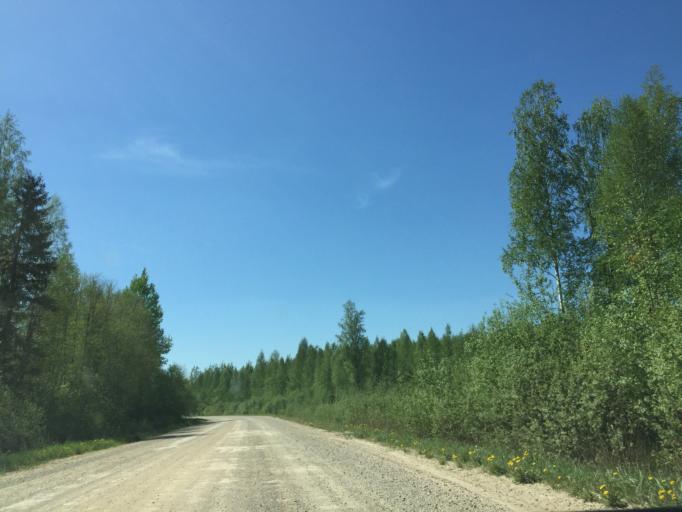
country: LV
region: Kegums
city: Kegums
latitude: 56.8787
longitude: 24.7810
